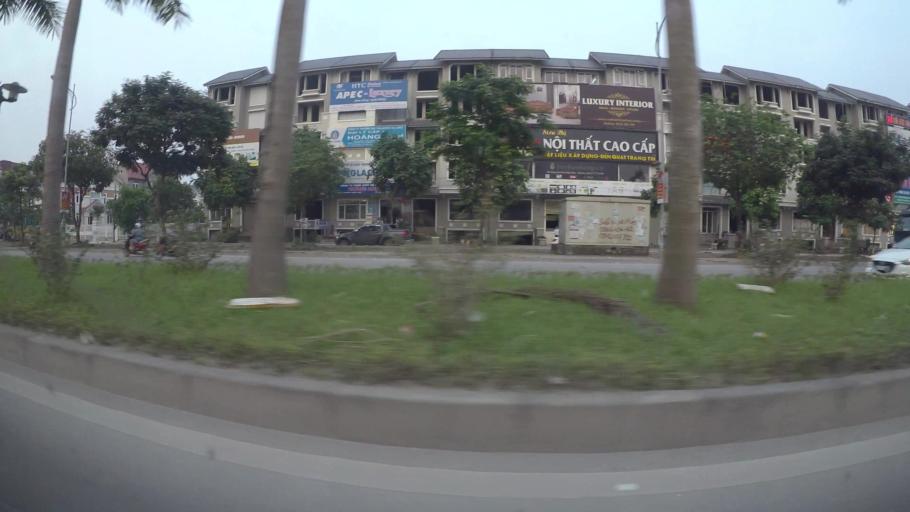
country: VN
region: Ha Noi
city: Cau Dien
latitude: 21.0071
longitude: 105.7315
